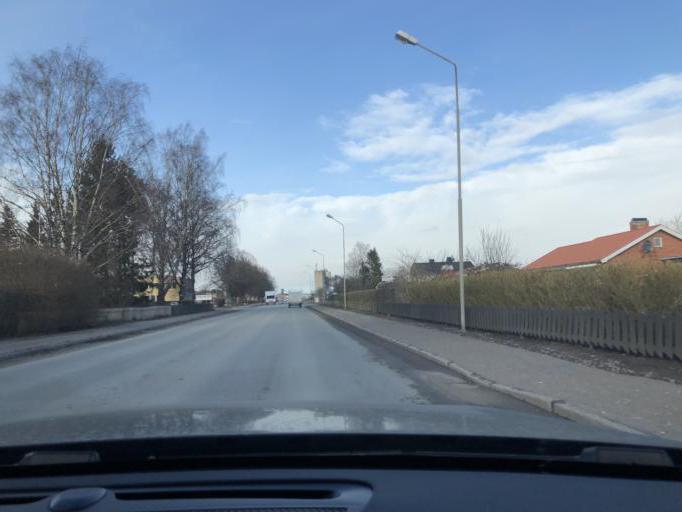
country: SE
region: Uppsala
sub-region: Tierps Kommun
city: Tierp
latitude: 60.3350
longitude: 17.5145
